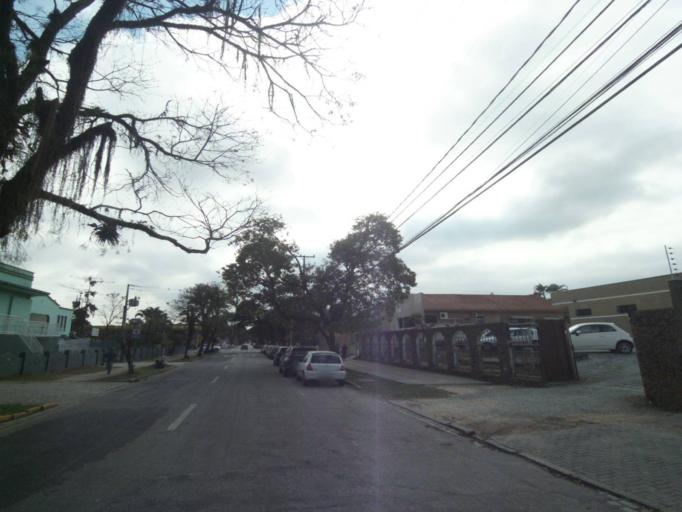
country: BR
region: Parana
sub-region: Paranagua
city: Paranagua
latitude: -25.5155
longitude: -48.5133
